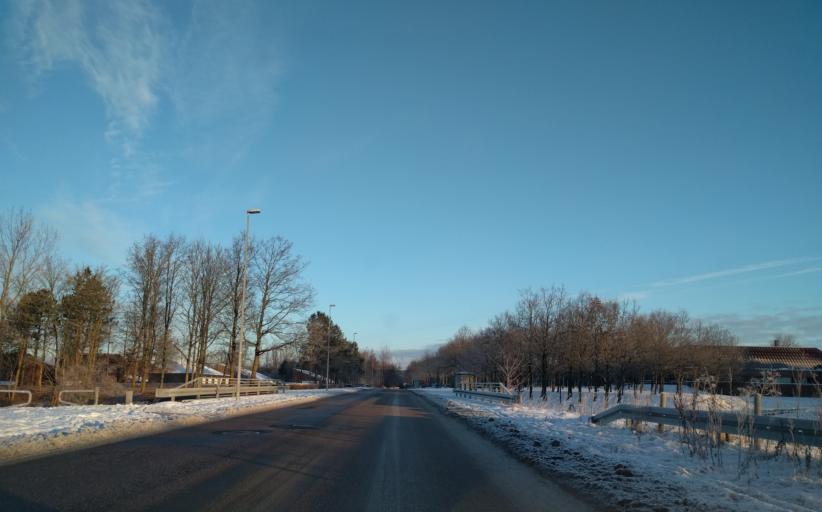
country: DK
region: North Denmark
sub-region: Alborg Kommune
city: Gistrup
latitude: 57.0157
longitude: 9.9843
